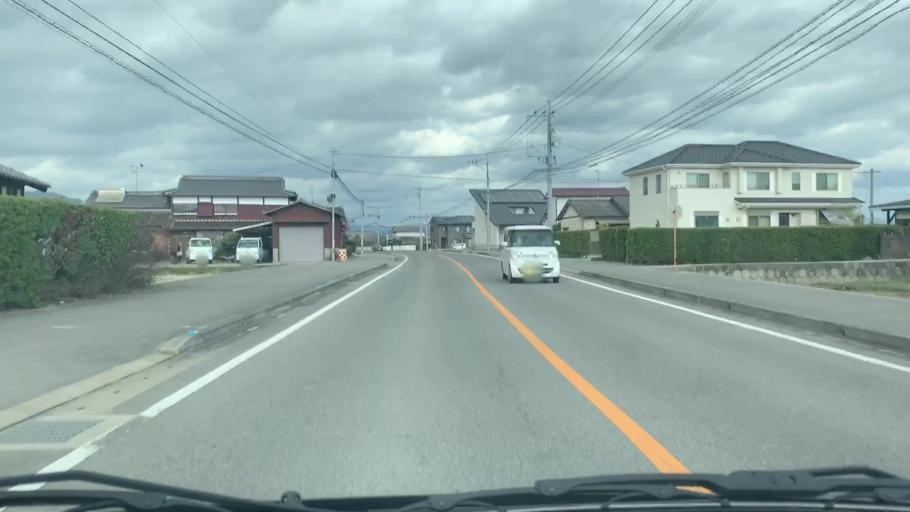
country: JP
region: Saga Prefecture
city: Saga-shi
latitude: 33.2440
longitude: 130.2377
